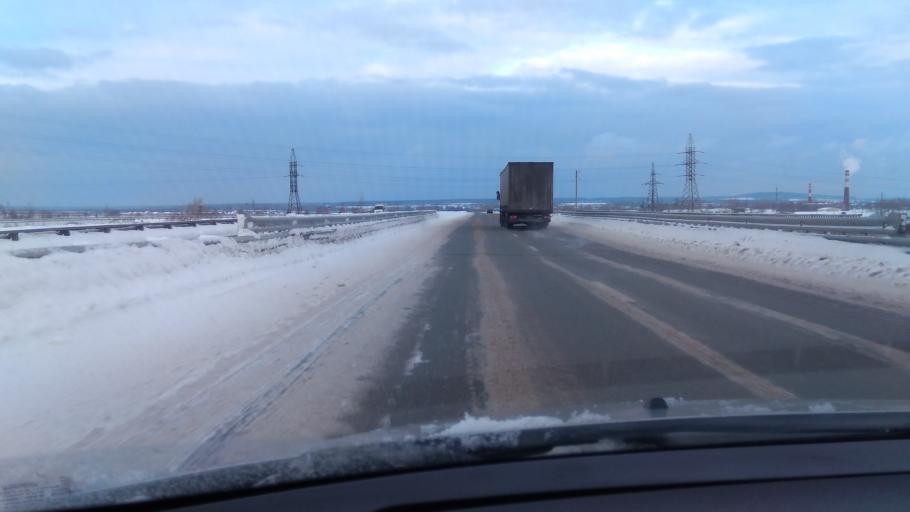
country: RU
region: Sverdlovsk
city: Tsementnyy
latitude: 57.4778
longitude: 60.1803
